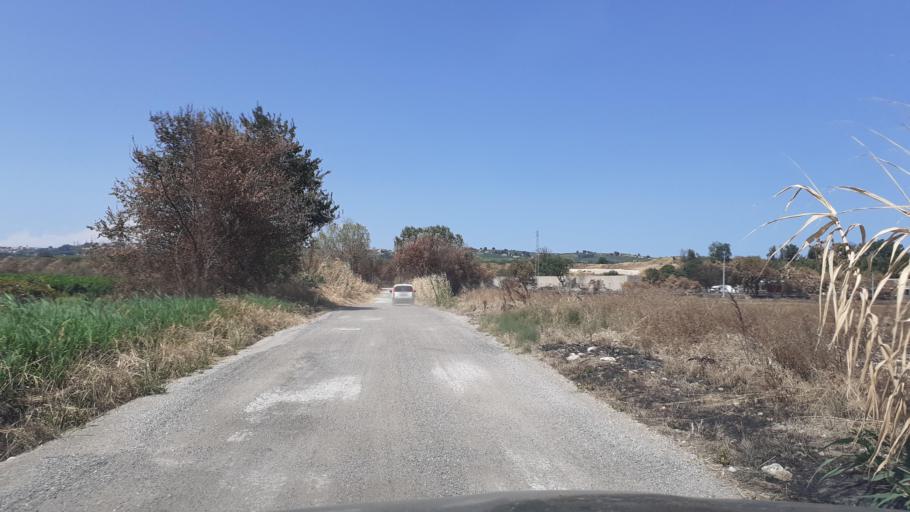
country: IT
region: Abruzzo
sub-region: Provincia di Chieti
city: Fossacesia
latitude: 42.2039
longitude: 14.4886
